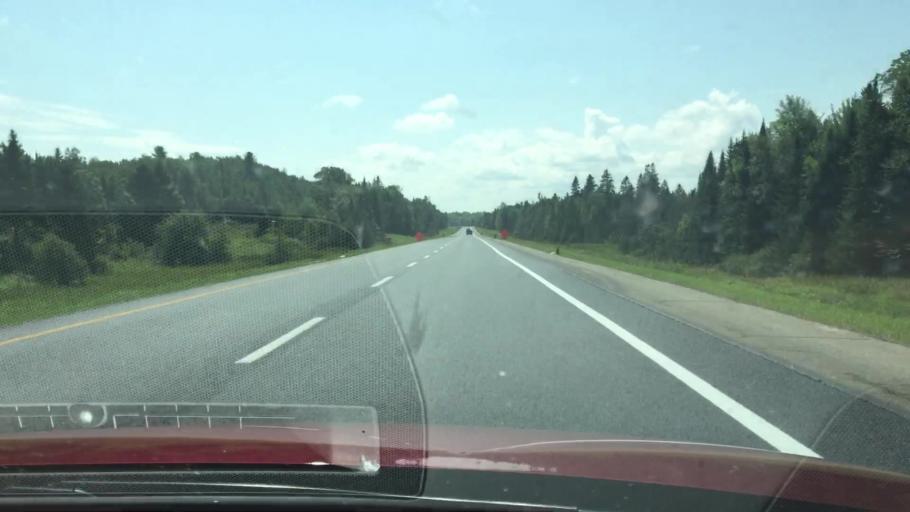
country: US
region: Maine
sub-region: Penobscot County
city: Patten
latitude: 45.8523
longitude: -68.4269
